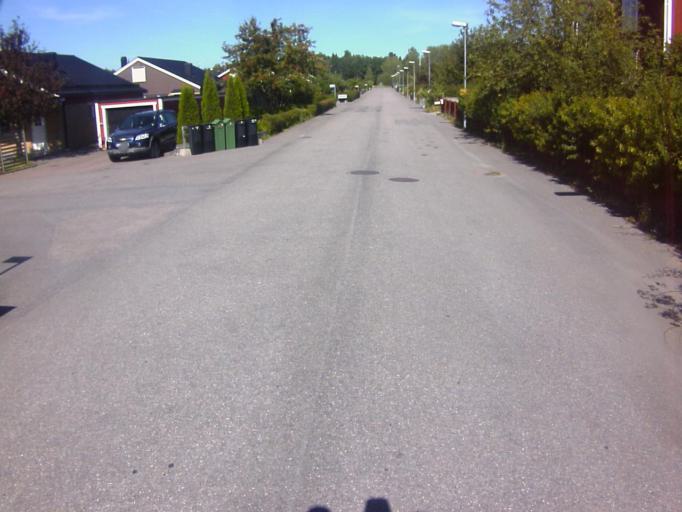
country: SE
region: Soedermanland
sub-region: Eskilstuna Kommun
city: Torshalla
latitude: 59.4370
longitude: 16.5296
